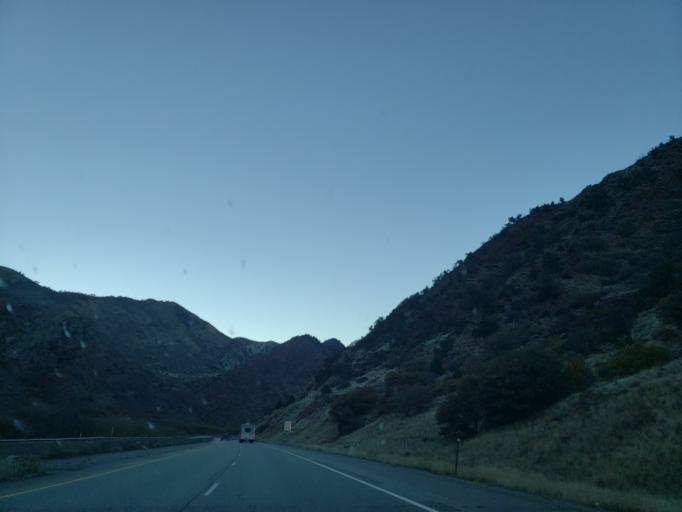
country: US
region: Colorado
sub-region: Garfield County
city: Glenwood Springs
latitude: 39.5658
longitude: -107.4175
